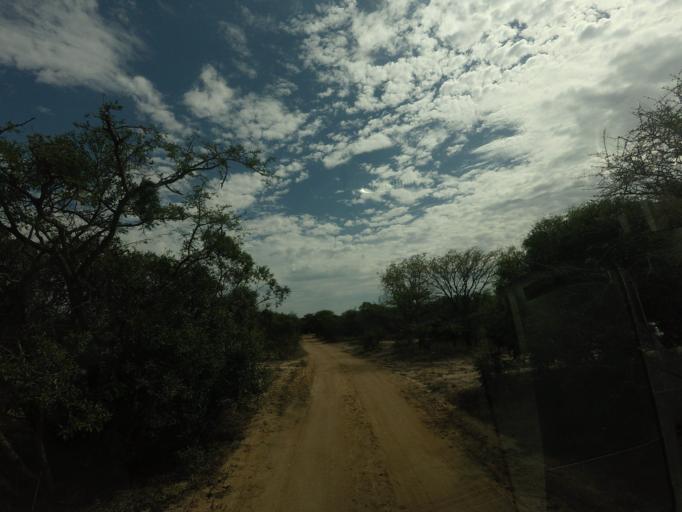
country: ZA
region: Limpopo
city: Thulamahashi
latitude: -24.5254
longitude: 31.1160
